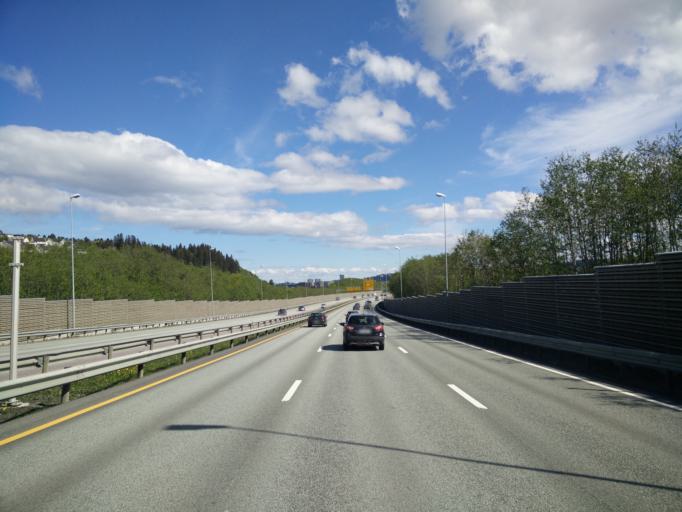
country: NO
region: Sor-Trondelag
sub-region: Trondheim
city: Trondheim
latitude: 63.3877
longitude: 10.3794
